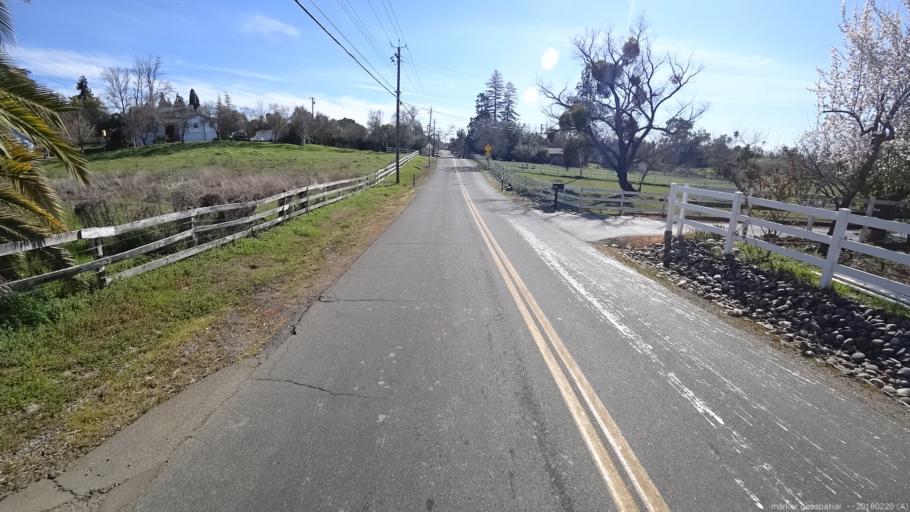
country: US
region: California
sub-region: Sacramento County
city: Orangevale
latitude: 38.7023
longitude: -121.2019
